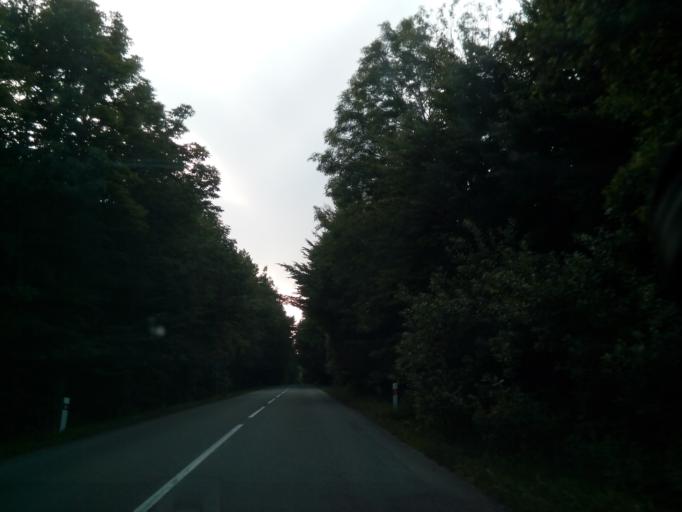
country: SK
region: Kosicky
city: Kosice
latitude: 48.6339
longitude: 21.4529
